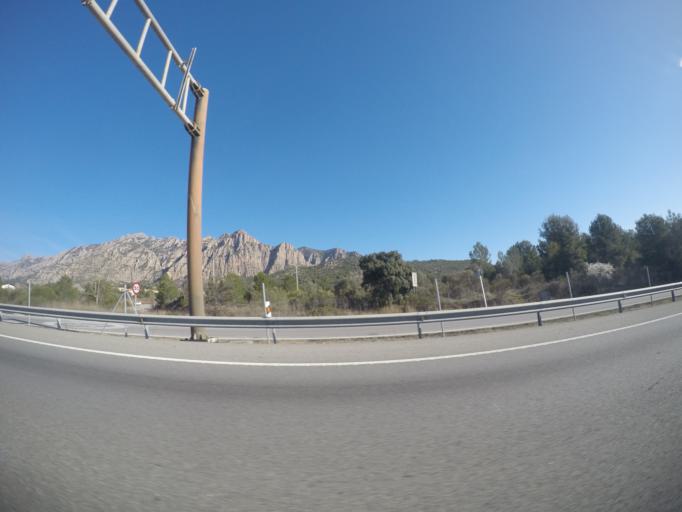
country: ES
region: Catalonia
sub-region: Provincia de Barcelona
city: Collbato
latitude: 41.5611
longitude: 1.8316
